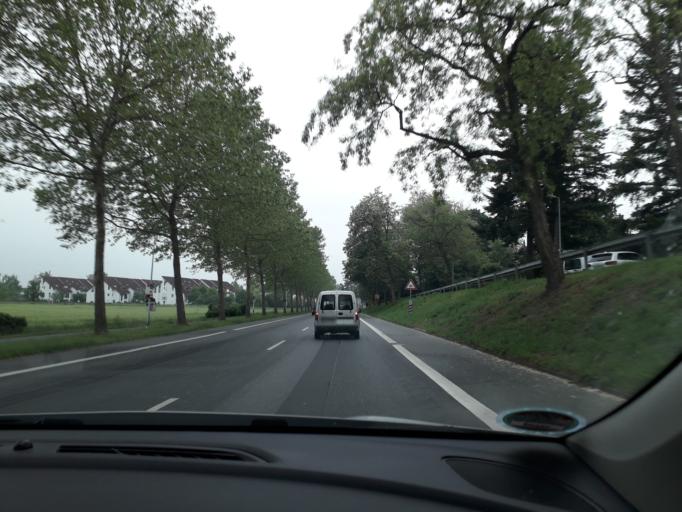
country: DE
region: Hesse
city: Pfungstadt
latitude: 49.8093
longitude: 8.6134
